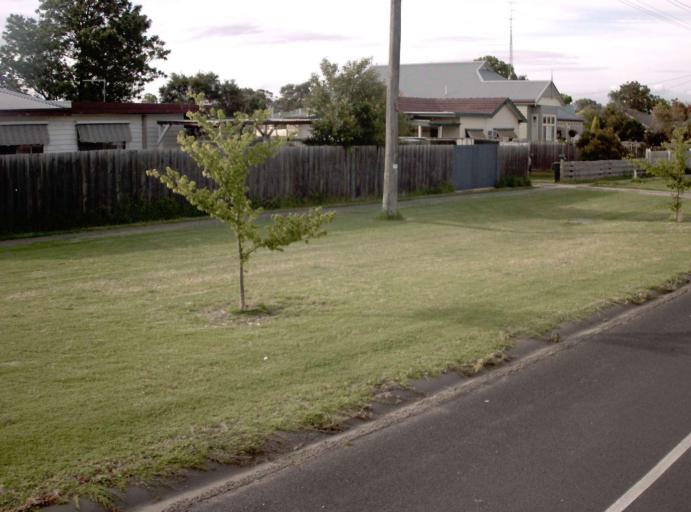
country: AU
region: Victoria
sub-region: Wellington
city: Sale
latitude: -37.9641
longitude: 146.9854
